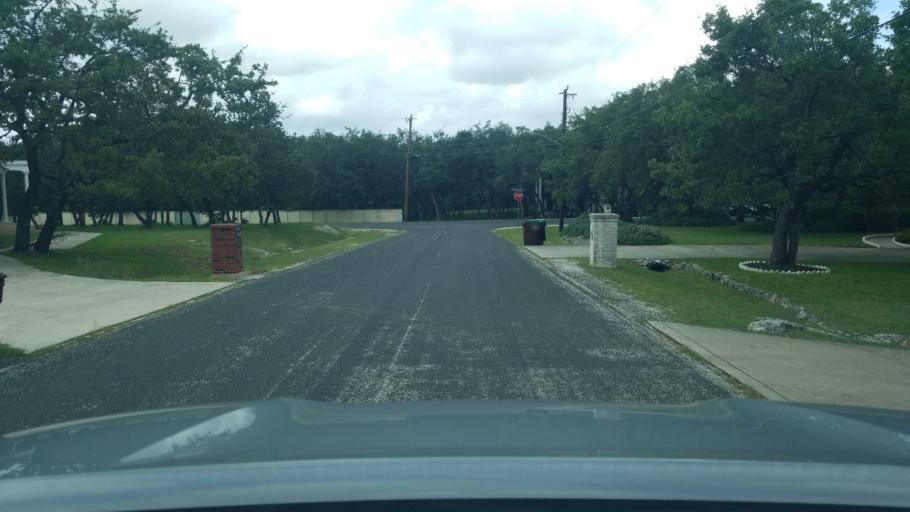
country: US
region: Texas
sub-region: Bexar County
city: Timberwood Park
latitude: 29.6921
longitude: -98.4989
